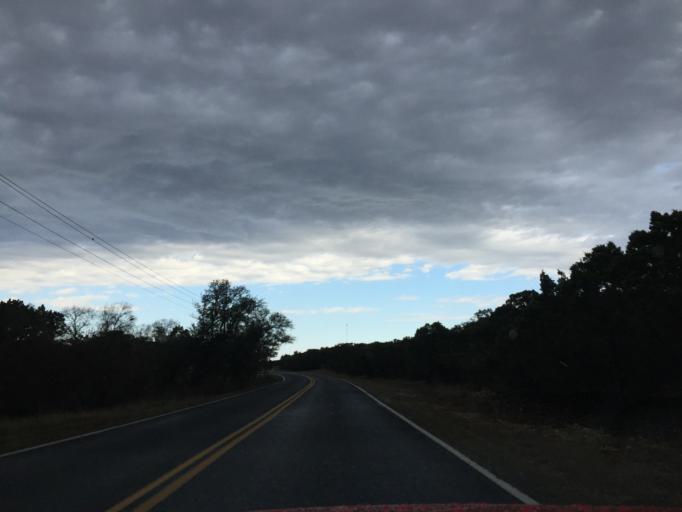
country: US
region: Texas
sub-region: Williamson County
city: Leander
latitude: 30.6114
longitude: -97.9377
